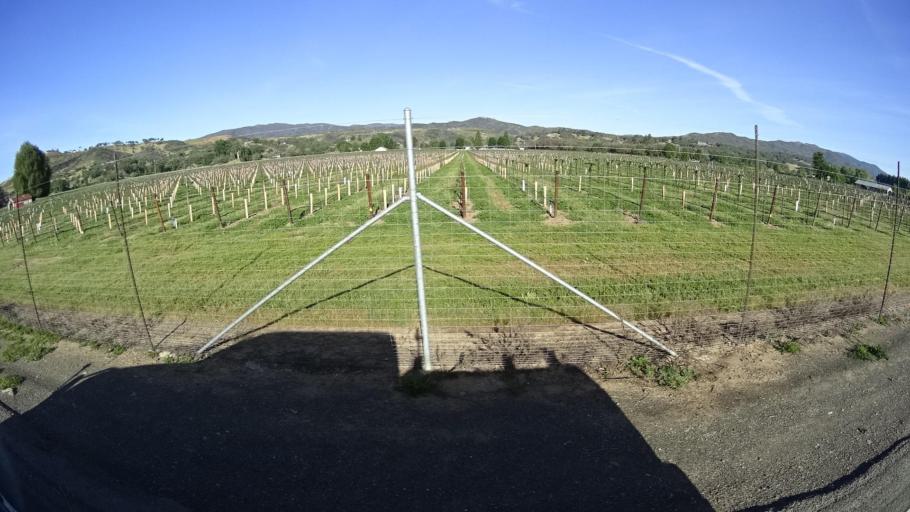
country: US
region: California
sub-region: Lake County
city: Lakeport
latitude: 39.0710
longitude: -122.9498
